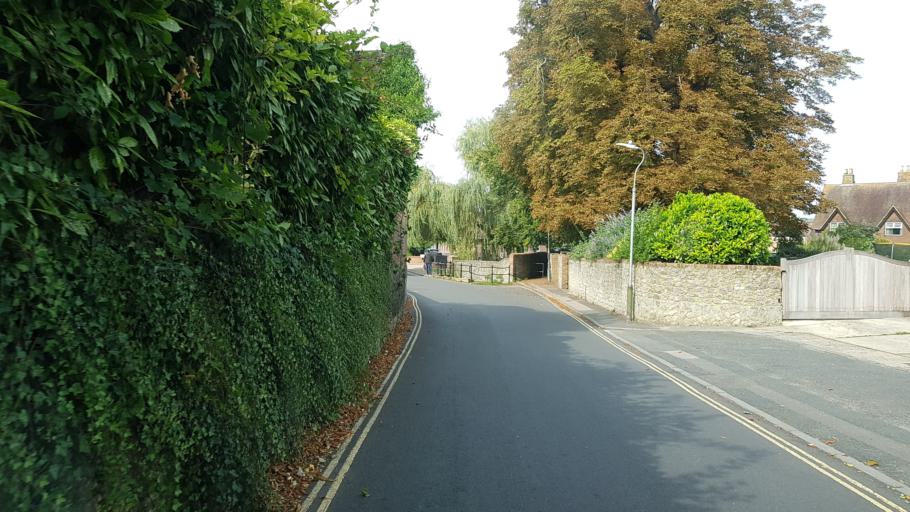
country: GB
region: England
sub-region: Kent
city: Larkfield
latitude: 51.2887
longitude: 0.4330
